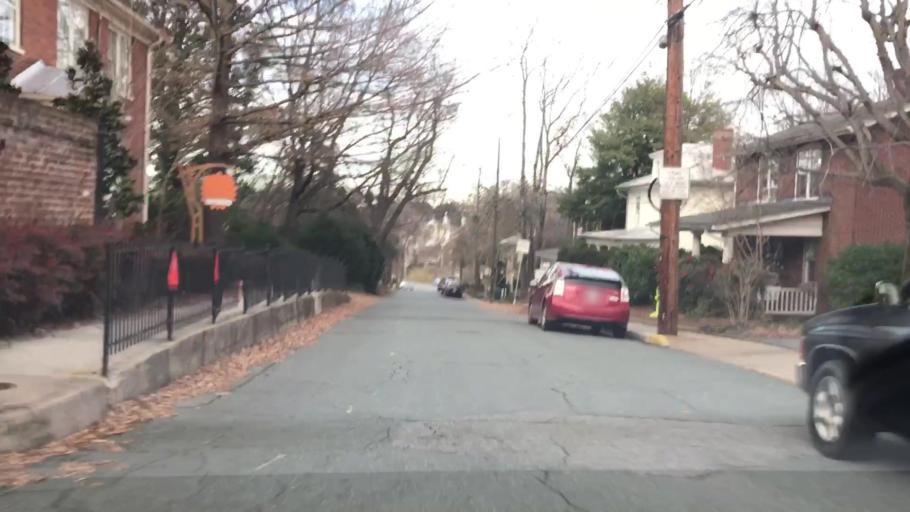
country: US
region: Virginia
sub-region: City of Charlottesville
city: Charlottesville
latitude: 38.0329
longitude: -78.4788
